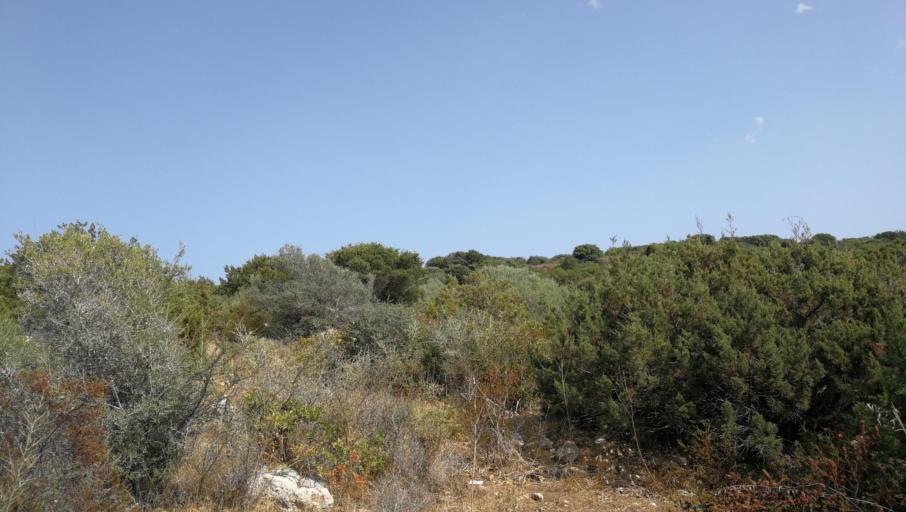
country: IT
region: Sardinia
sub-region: Provincia di Olbia-Tempio
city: Golfo Aranci
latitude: 41.0125
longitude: 9.5872
